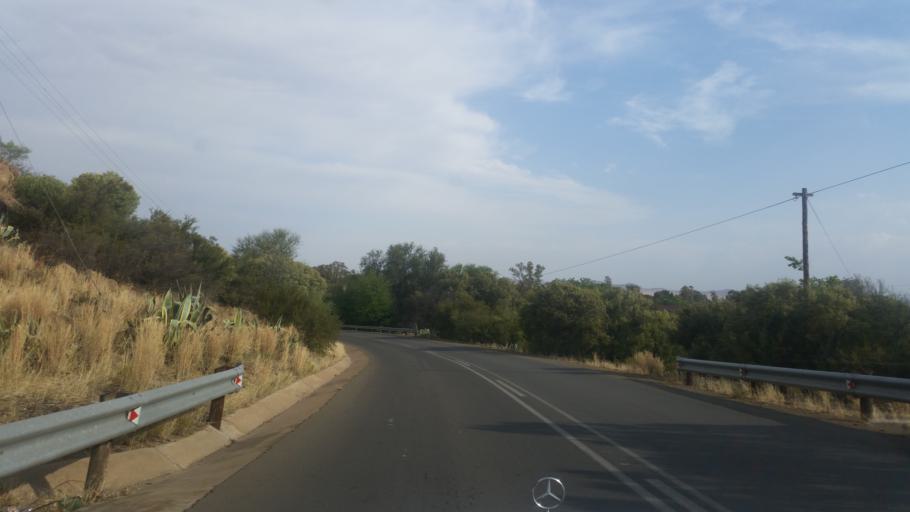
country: ZA
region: Orange Free State
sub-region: Xhariep District Municipality
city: Trompsburg
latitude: -30.4930
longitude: 25.9665
